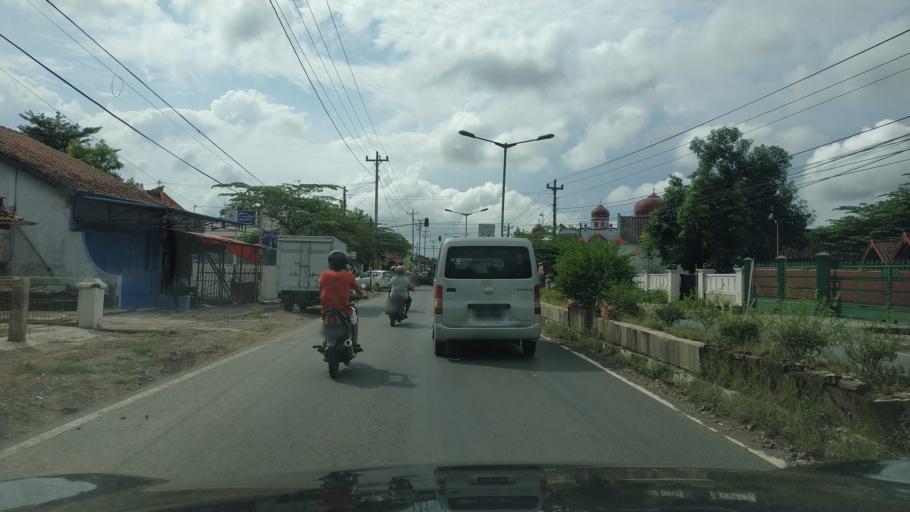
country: ID
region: Central Java
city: Pemalang
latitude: -6.9176
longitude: 109.3834
